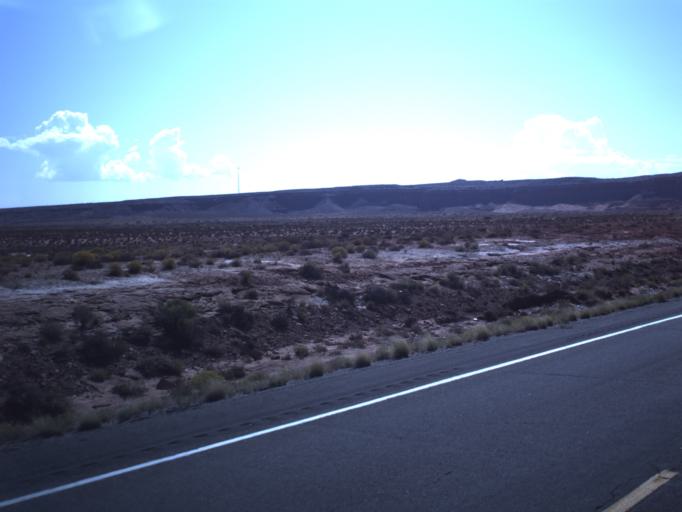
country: US
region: Utah
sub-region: San Juan County
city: Blanding
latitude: 37.0006
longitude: -109.6097
